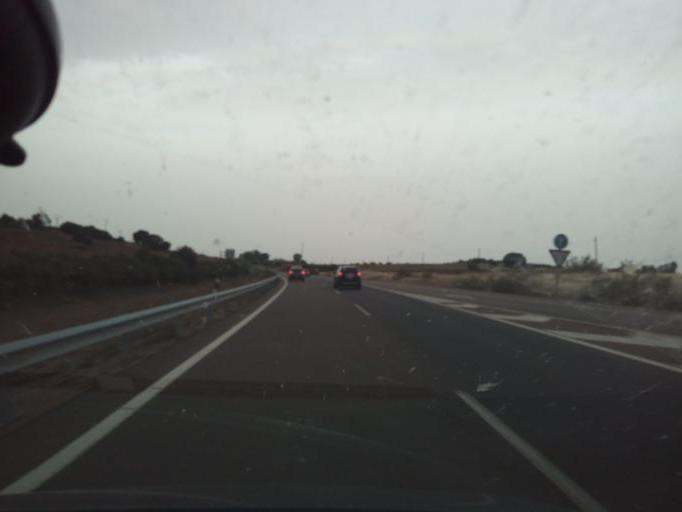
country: ES
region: Extremadura
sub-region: Provincia de Badajoz
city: San Pedro de Merida
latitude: 38.9471
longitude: -6.1900
